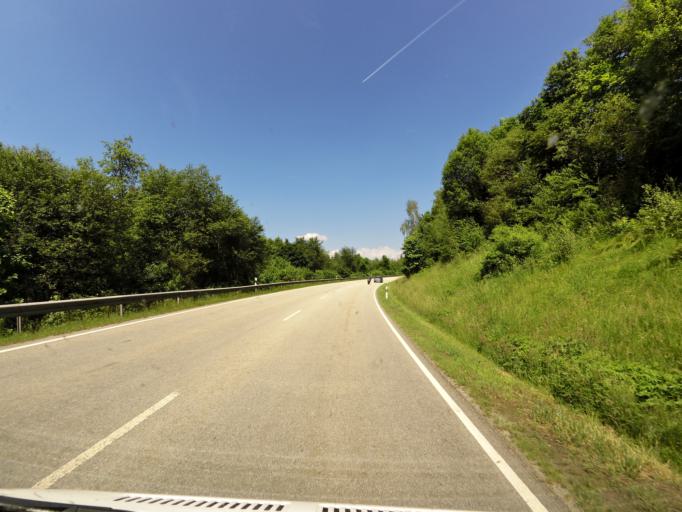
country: DE
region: Bavaria
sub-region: Lower Bavaria
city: Roehrnbach
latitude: 48.7418
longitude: 13.5154
